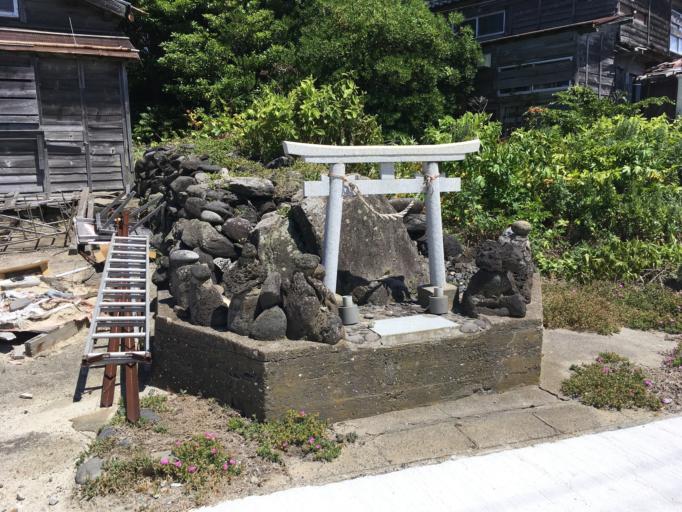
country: JP
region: Ishikawa
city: Nanao
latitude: 37.8505
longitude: 136.9211
